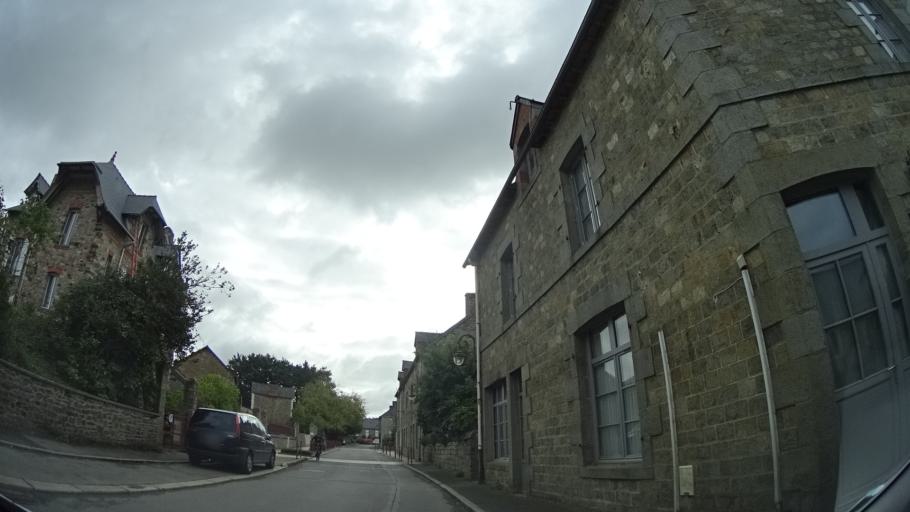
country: FR
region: Brittany
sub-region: Departement d'Ille-et-Vilaine
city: Montreuil-sur-Ille
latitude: 48.3070
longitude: -1.6697
